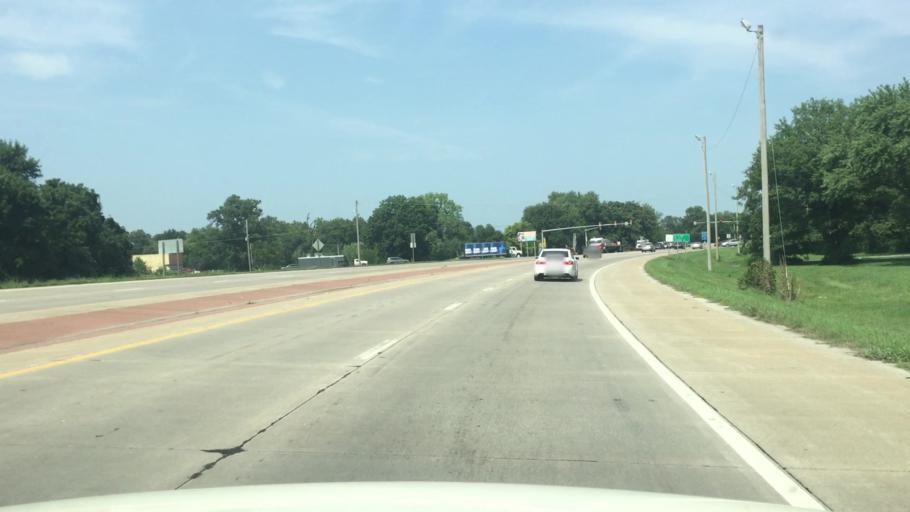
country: US
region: Kansas
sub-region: Crawford County
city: Pittsburg
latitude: 37.4094
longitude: -94.7246
